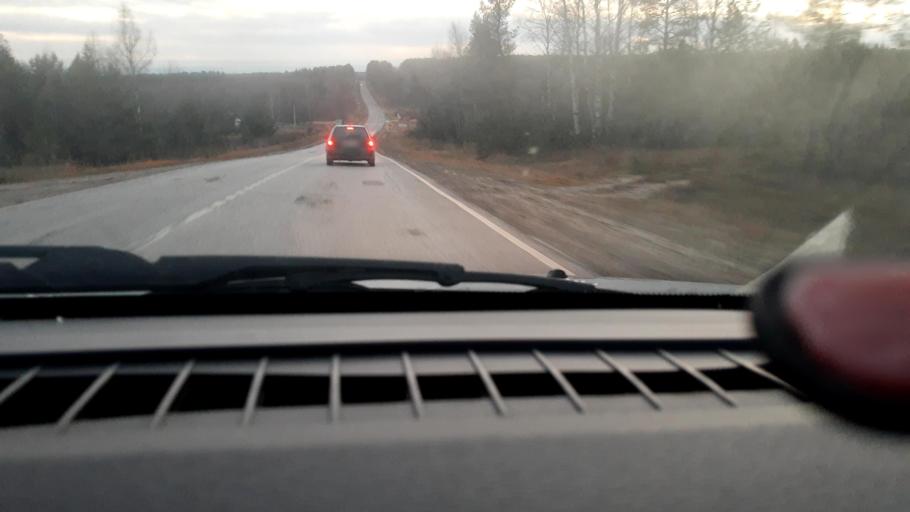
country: RU
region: Nizjnij Novgorod
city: Krasnyye Baki
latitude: 57.0461
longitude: 45.1337
